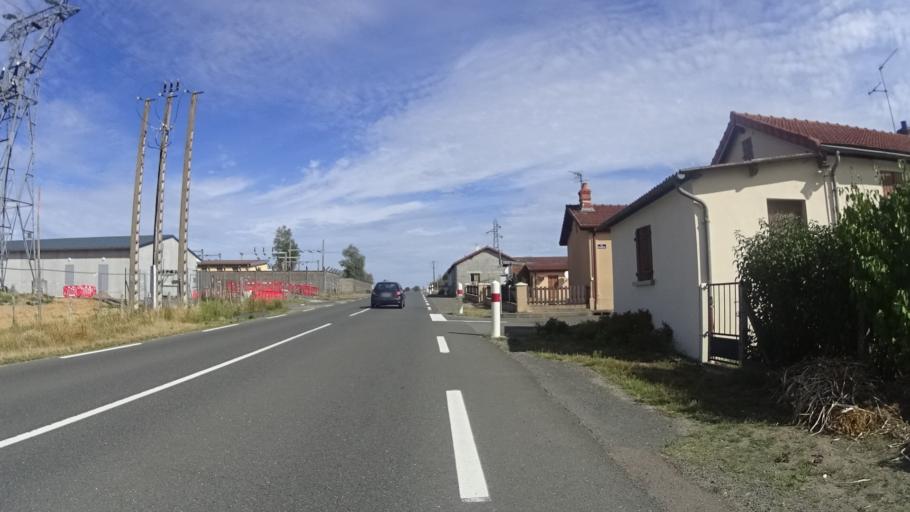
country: FR
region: Bourgogne
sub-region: Departement de Saone-et-Loire
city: Bourbon-Lancy
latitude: 46.6214
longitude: 3.7392
